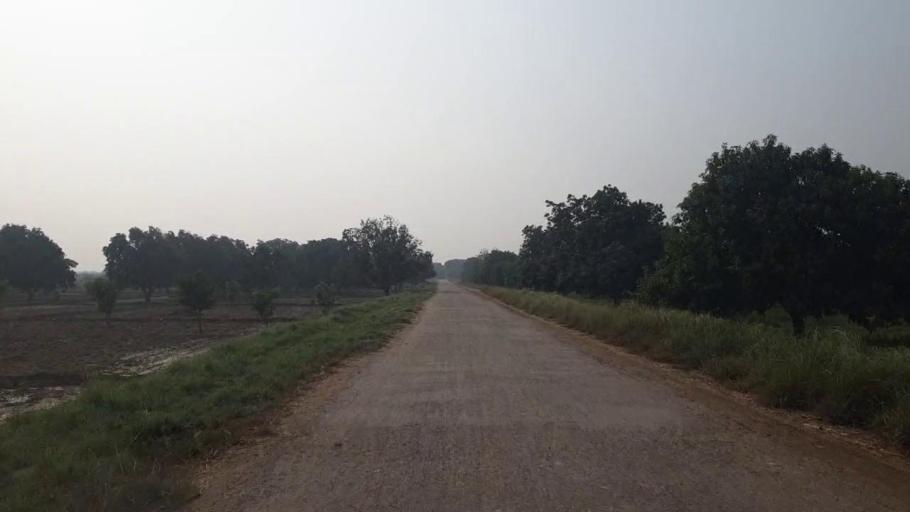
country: PK
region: Sindh
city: Tando Jam
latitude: 25.3274
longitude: 68.5181
